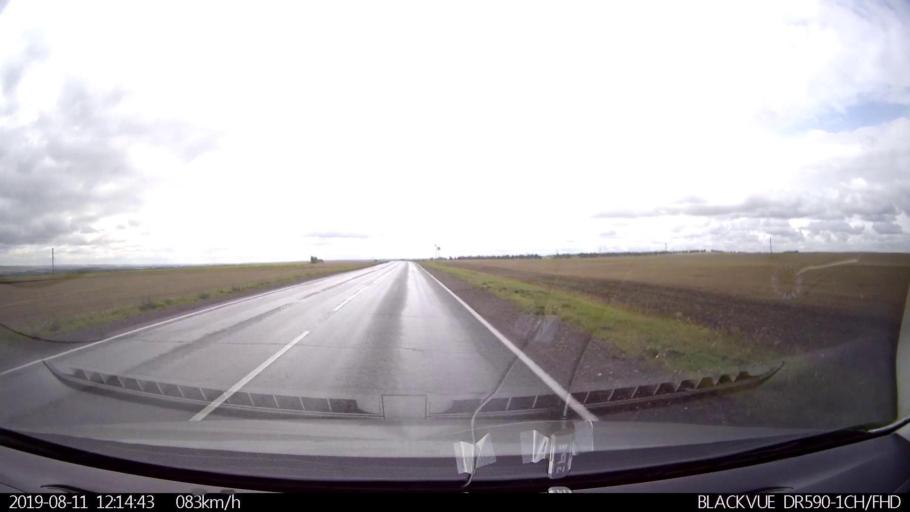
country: RU
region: Ulyanovsk
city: Ignatovka
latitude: 53.9495
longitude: 47.9763
